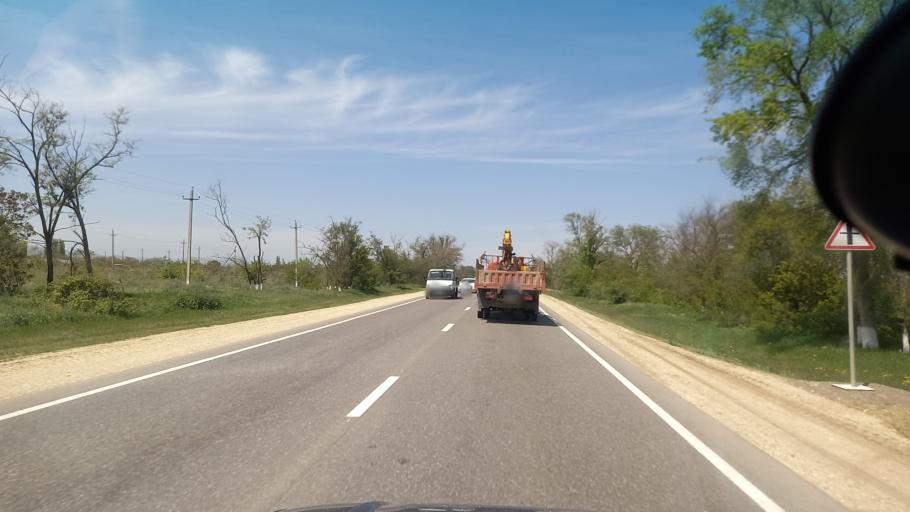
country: RU
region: Dagestan
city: Achisu
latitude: 42.6667
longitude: 47.7113
